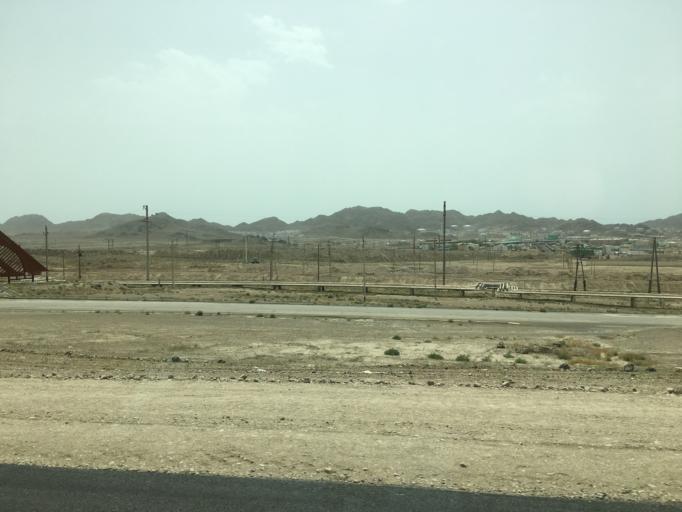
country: TM
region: Balkan
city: Turkmenbasy
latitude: 40.0135
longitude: 53.0748
